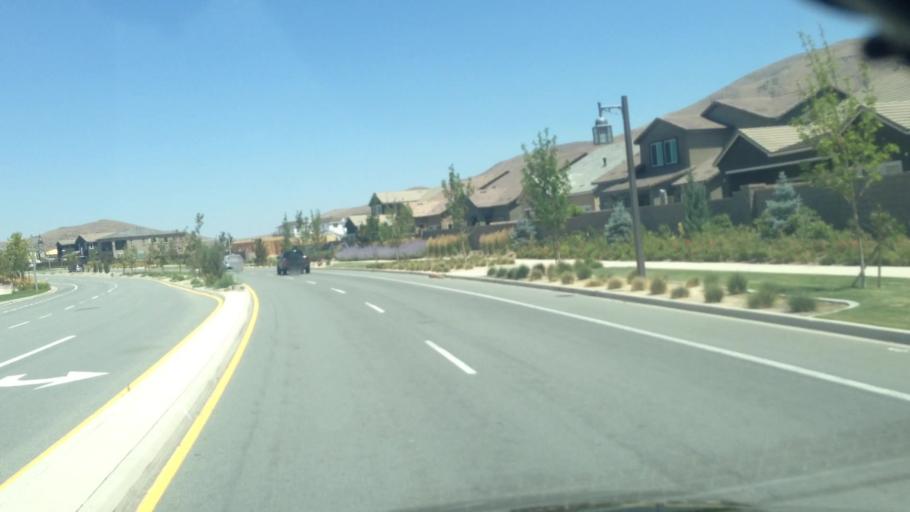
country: US
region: Nevada
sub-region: Washoe County
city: Sparks
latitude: 39.4439
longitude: -119.7270
